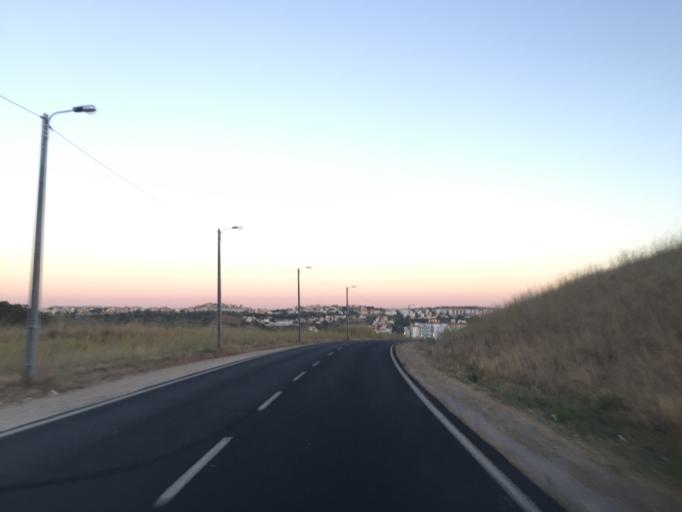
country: PT
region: Lisbon
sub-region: Odivelas
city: Povoa de Santo Adriao
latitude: 38.8093
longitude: -9.1715
